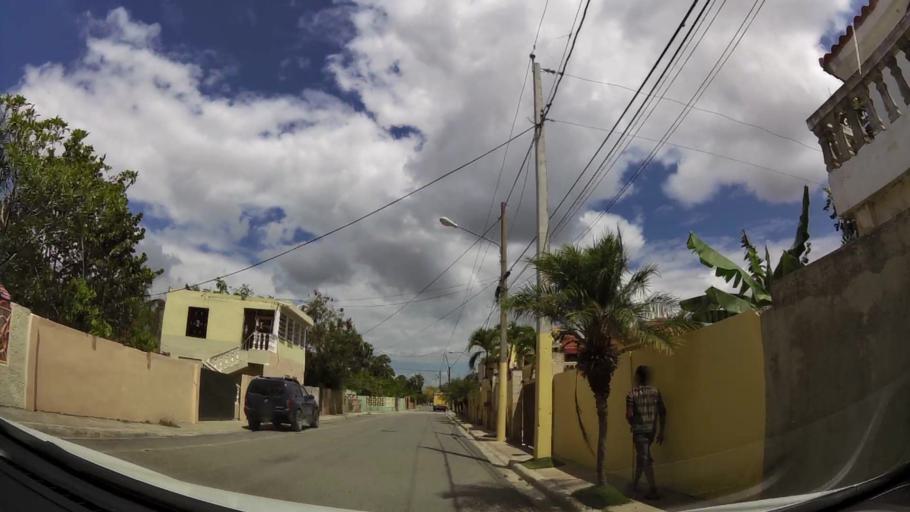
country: DO
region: Santo Domingo
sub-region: Santo Domingo
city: Boca Chica
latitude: 18.4502
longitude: -69.6559
